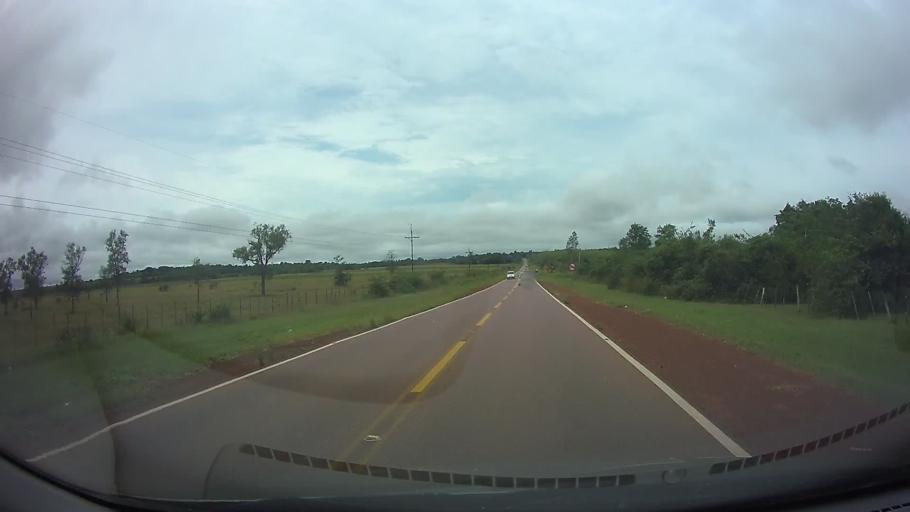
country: PY
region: Paraguari
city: Acahay
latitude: -25.8373
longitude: -57.1510
